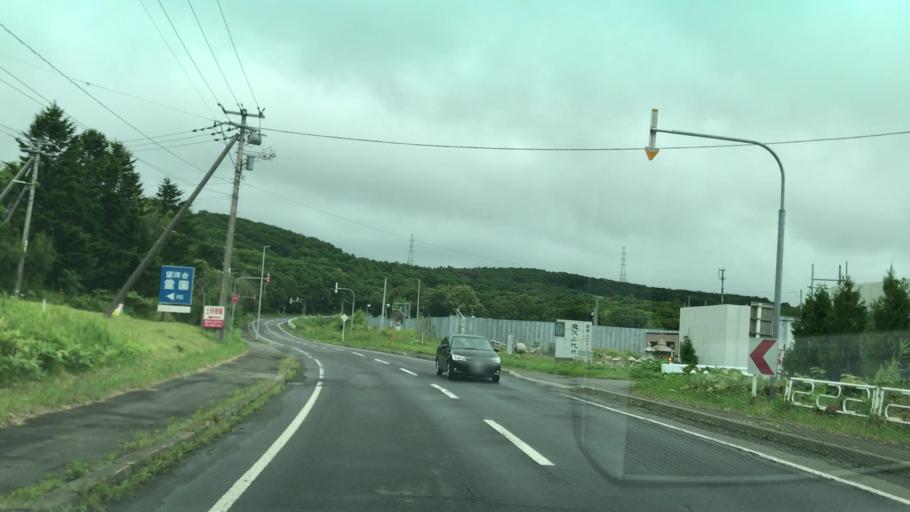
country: JP
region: Hokkaido
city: Muroran
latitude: 42.3917
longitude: 141.0022
